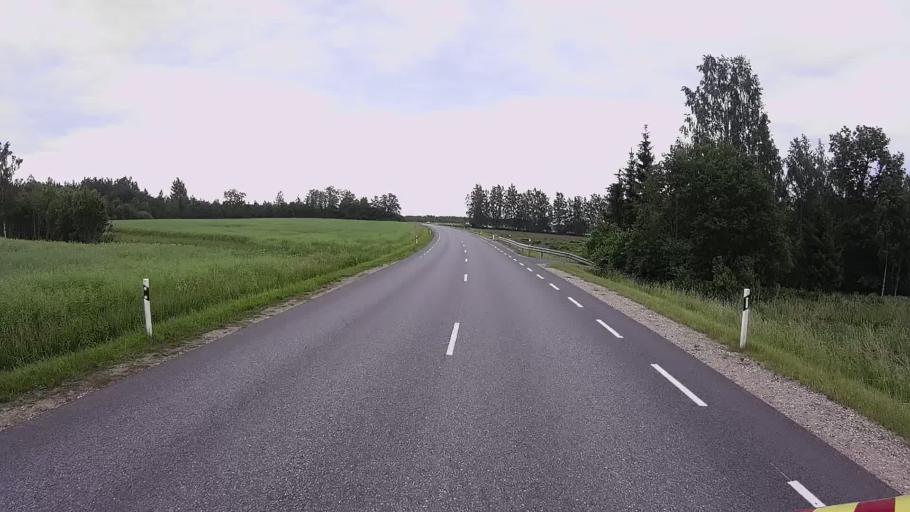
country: EE
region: Viljandimaa
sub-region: Karksi vald
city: Karksi-Nuia
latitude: 58.1619
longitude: 25.5882
